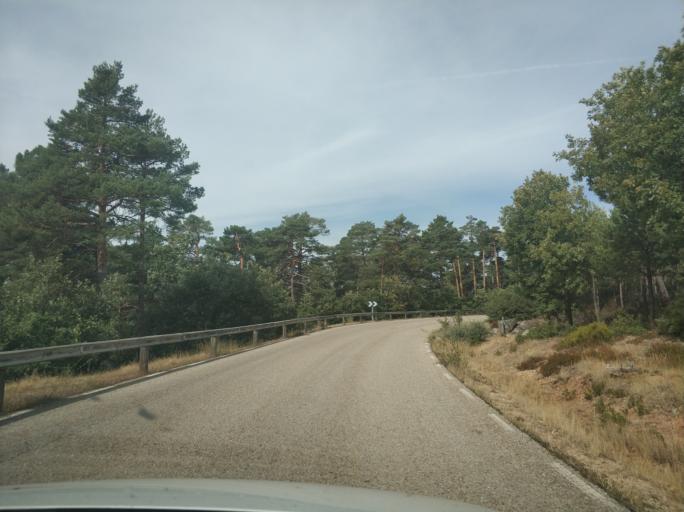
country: ES
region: Castille and Leon
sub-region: Provincia de Soria
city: Duruelo de la Sierra
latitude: 41.9079
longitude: -2.9456
